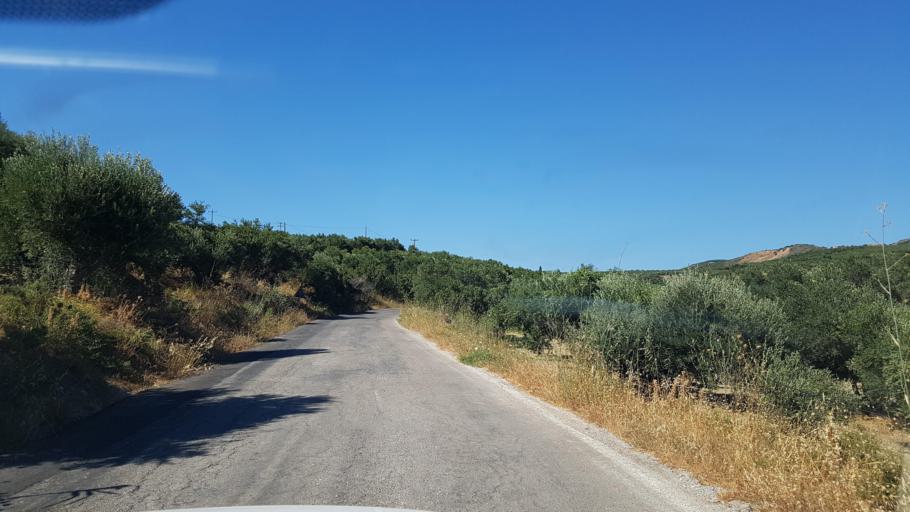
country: GR
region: Crete
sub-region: Nomos Chanias
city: Kissamos
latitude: 35.4970
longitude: 23.7221
